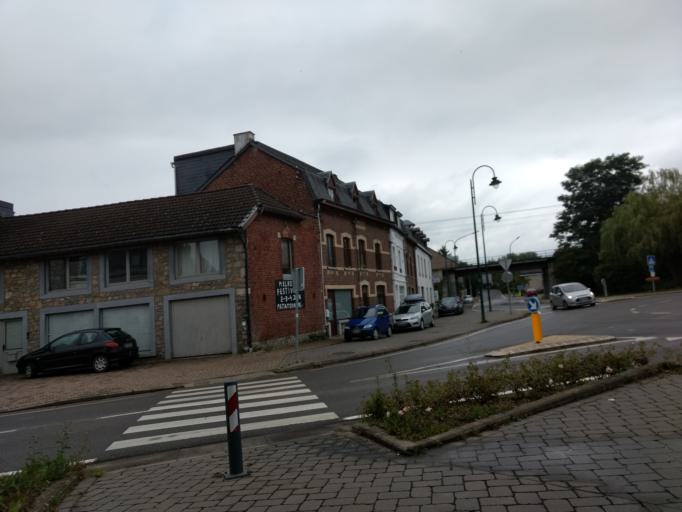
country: BE
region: Wallonia
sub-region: Province du Luxembourg
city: Hotton
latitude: 50.2822
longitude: 5.4403
